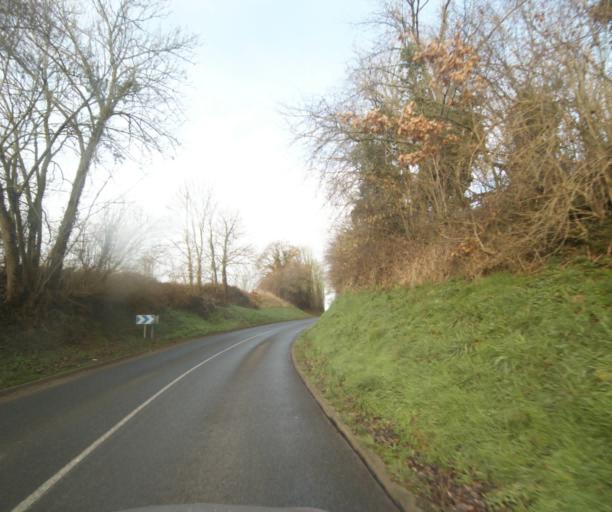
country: FR
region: Nord-Pas-de-Calais
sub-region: Departement du Nord
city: Artres
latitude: 50.2929
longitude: 3.5339
